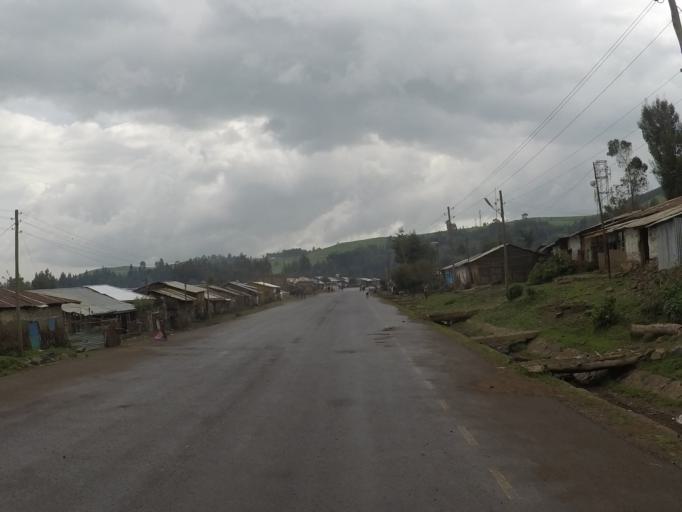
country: ET
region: Amhara
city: Dabat
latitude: 13.0674
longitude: 37.8263
